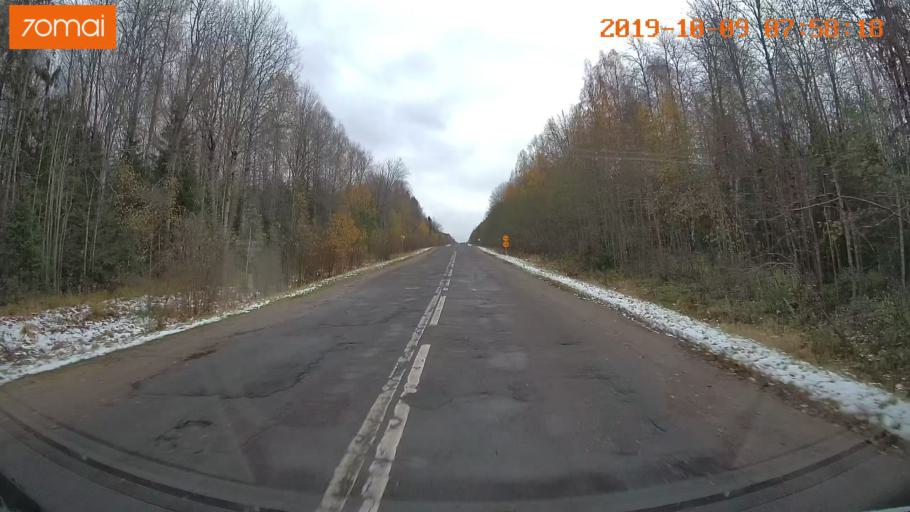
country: RU
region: Jaroslavl
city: Kukoboy
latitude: 58.6970
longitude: 39.9638
